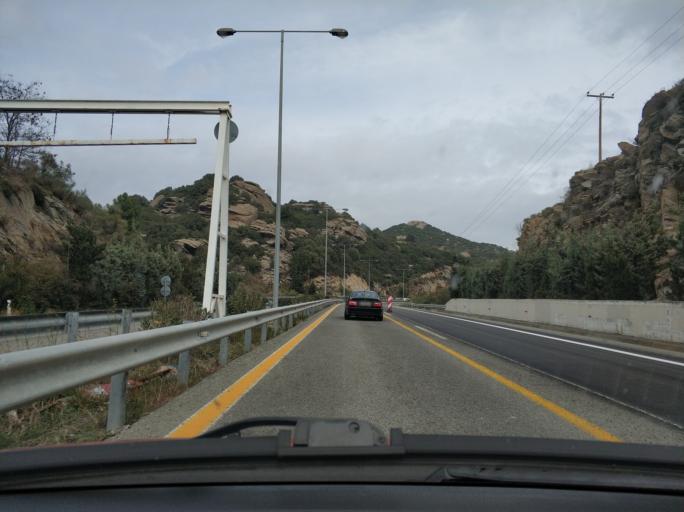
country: GR
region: East Macedonia and Thrace
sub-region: Nomos Kavalas
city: Palaio Tsifliki
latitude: 40.9127
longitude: 24.3591
